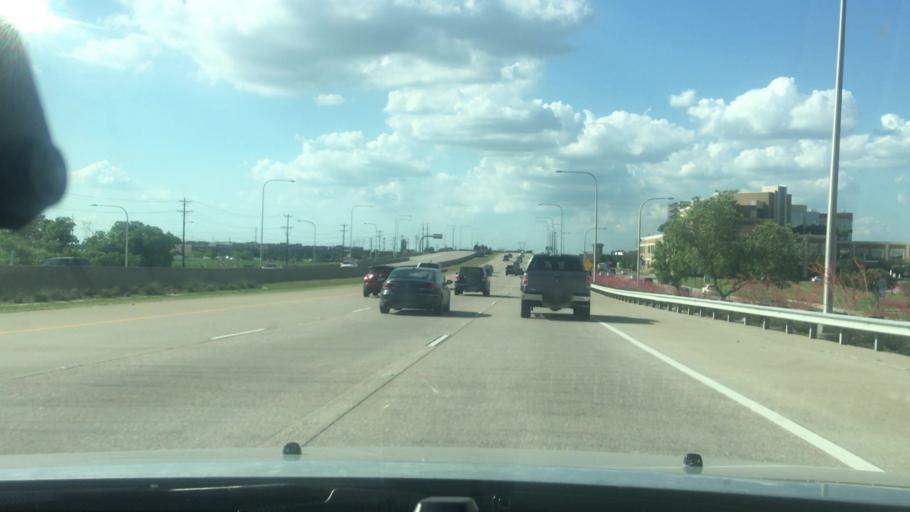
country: US
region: Texas
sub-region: Collin County
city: Frisco
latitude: 33.1480
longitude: -96.8393
